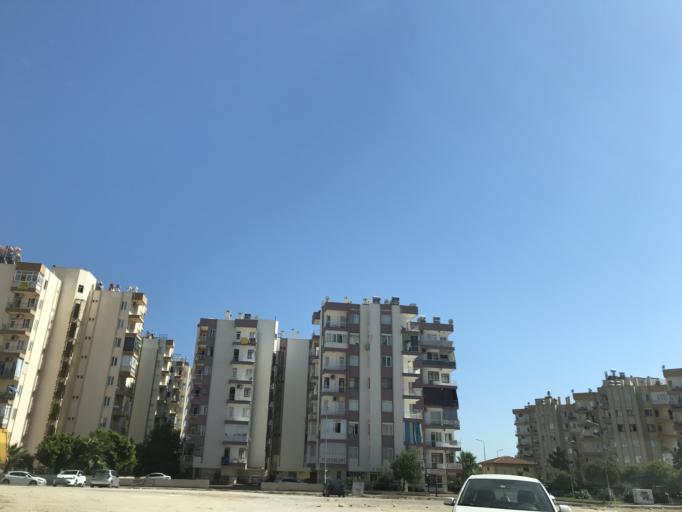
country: TR
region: Antalya
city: Antalya
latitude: 36.9023
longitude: 30.6567
